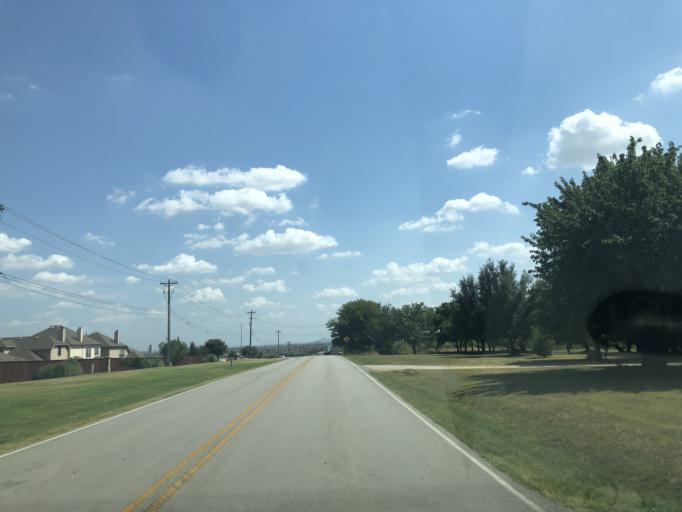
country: US
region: Texas
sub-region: Tarrant County
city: Haslet
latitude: 32.9259
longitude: -97.3316
